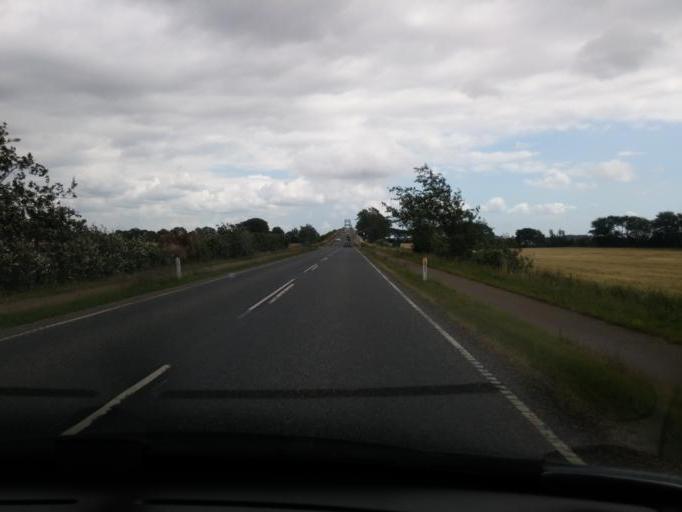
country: DK
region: South Denmark
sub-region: Langeland Kommune
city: Rudkobing
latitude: 54.9519
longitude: 10.6929
